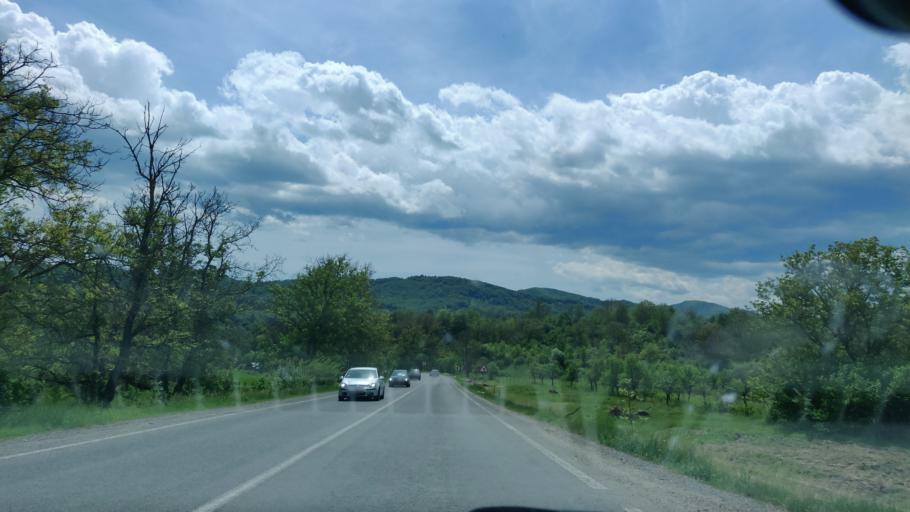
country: RO
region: Vrancea
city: Matacina
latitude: 45.8973
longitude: 26.8506
